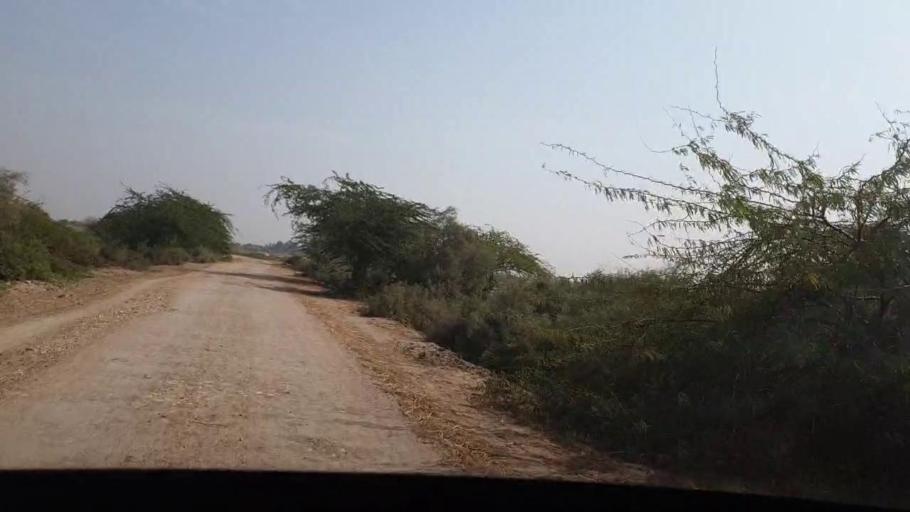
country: PK
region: Sindh
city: Chuhar Jamali
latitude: 24.2691
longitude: 67.9348
